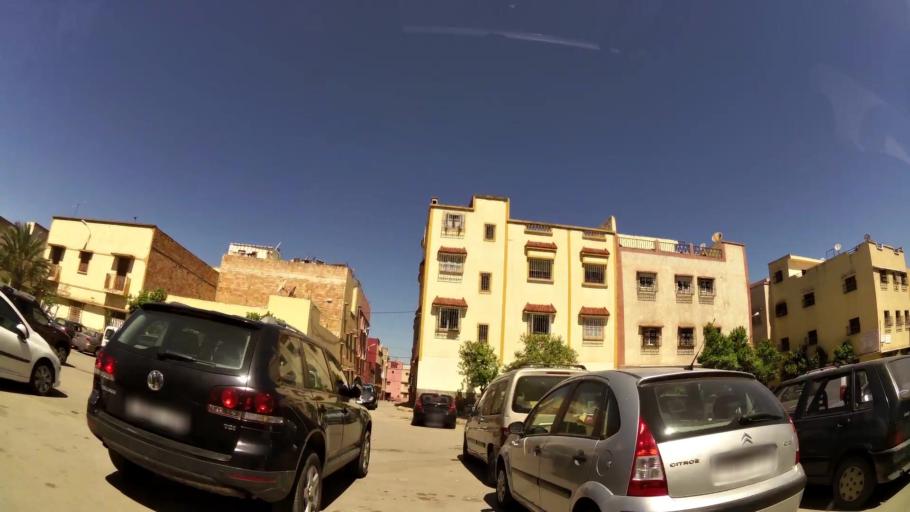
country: MA
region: Meknes-Tafilalet
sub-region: Meknes
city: Meknes
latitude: 33.9054
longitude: -5.5264
